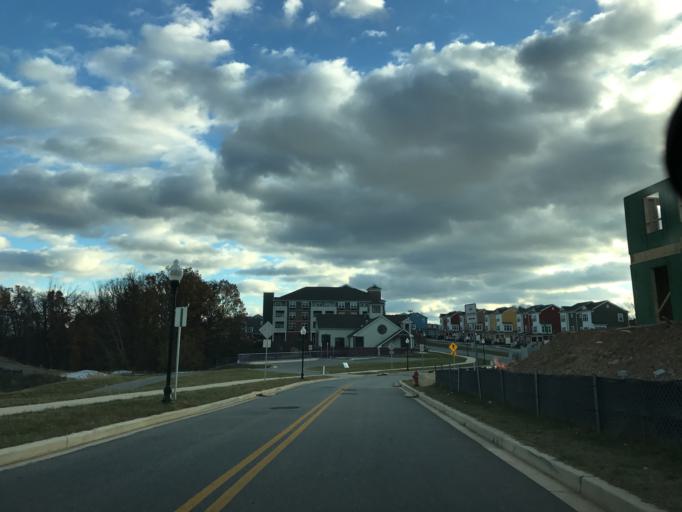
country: US
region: Maryland
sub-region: Baltimore County
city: Rosedale
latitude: 39.3138
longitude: -76.5591
